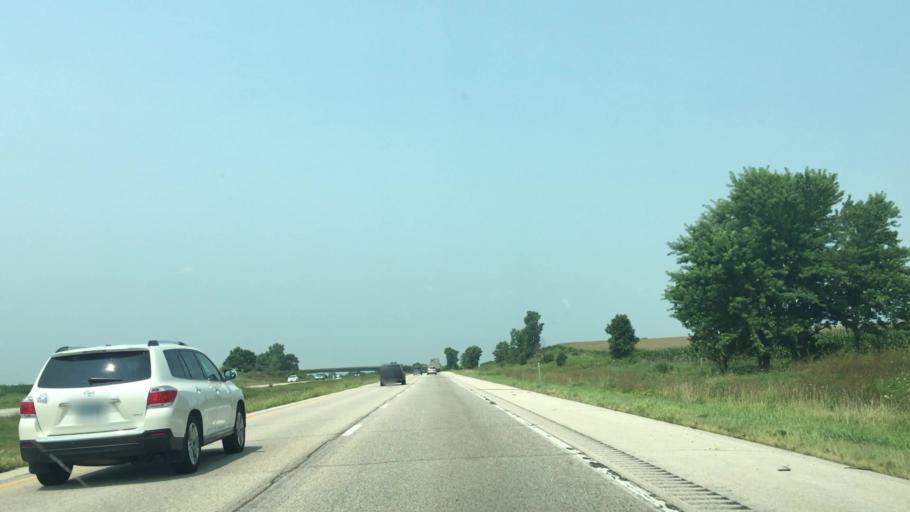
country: US
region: Iowa
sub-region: Linn County
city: Center Point
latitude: 42.1532
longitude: -91.7509
